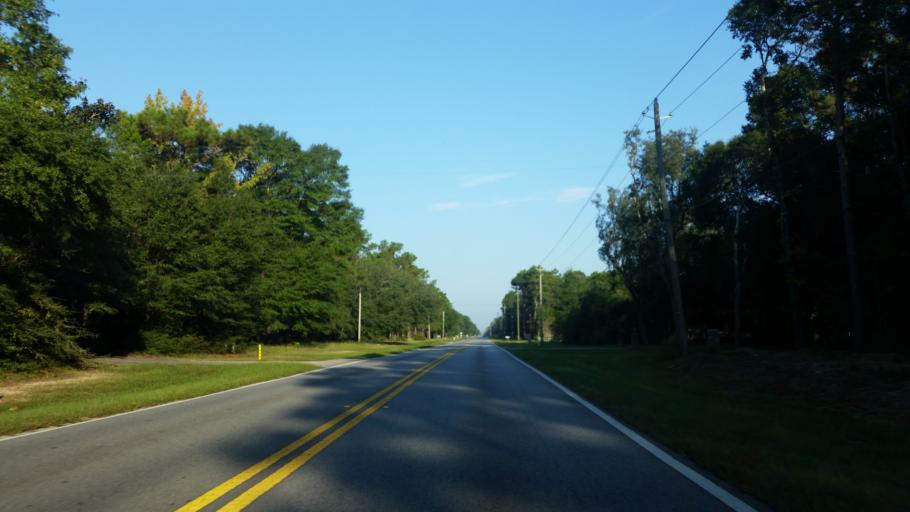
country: US
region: Florida
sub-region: Santa Rosa County
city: Milton
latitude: 30.6470
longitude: -87.0610
